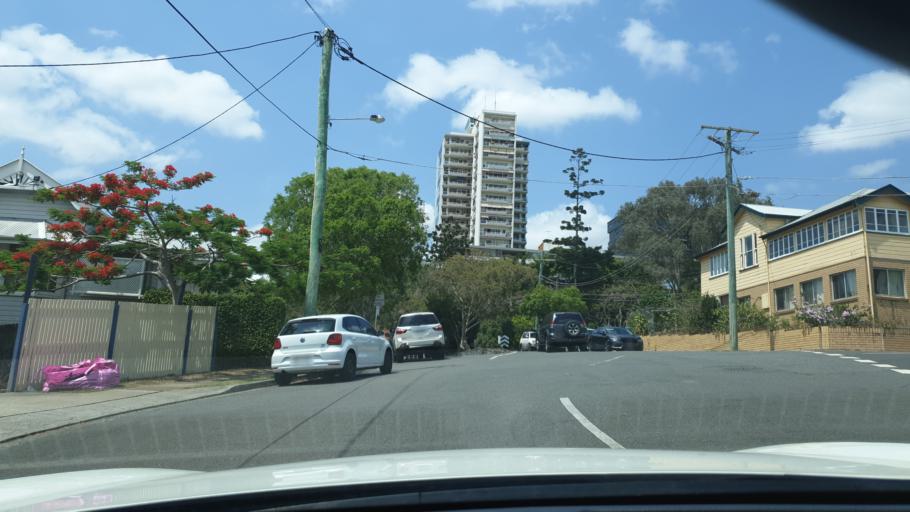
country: AU
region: Queensland
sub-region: Brisbane
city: South Brisbane
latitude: -27.4851
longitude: 153.0186
